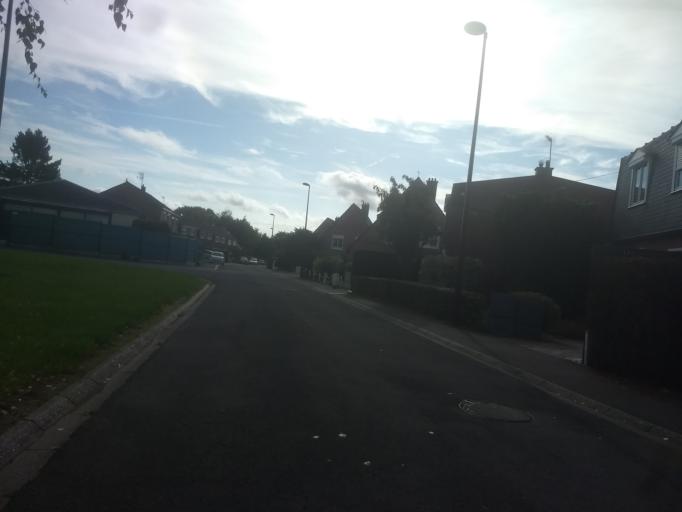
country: FR
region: Nord-Pas-de-Calais
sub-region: Departement du Pas-de-Calais
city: Dainville
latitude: 50.2854
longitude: 2.7314
